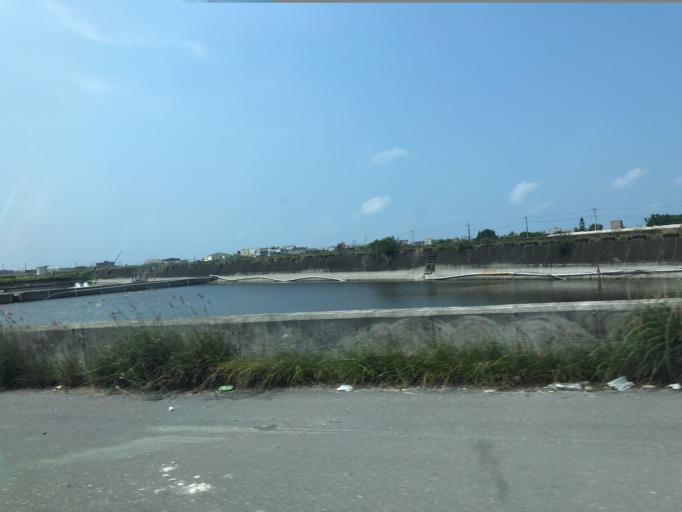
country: TW
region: Taiwan
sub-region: Chiayi
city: Taibao
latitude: 23.4709
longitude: 120.1531
